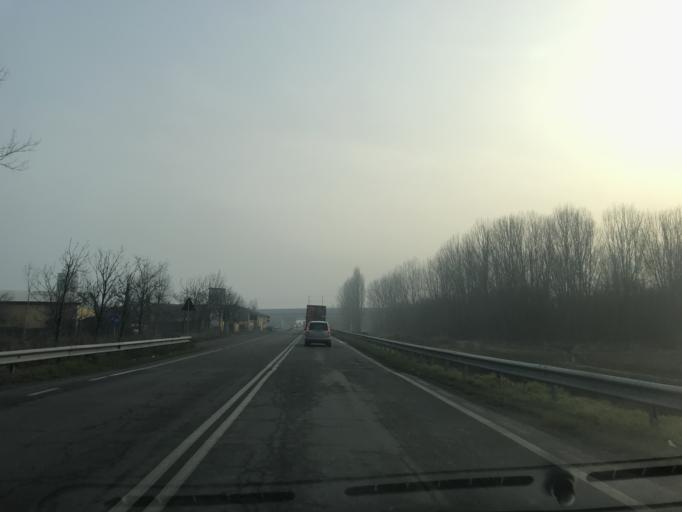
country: IT
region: Lombardy
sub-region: Provincia di Lodi
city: Villanova del Sillaro
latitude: 45.2414
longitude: 9.5009
